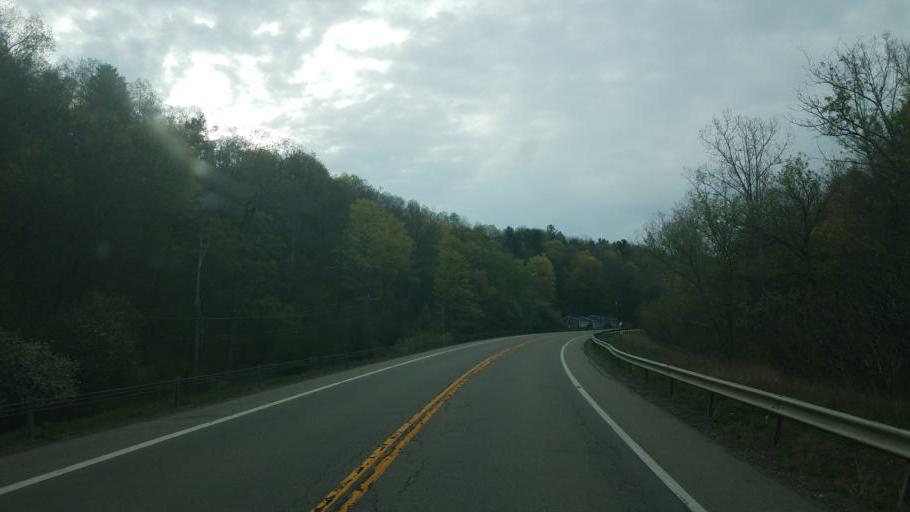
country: US
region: New York
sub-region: Steuben County
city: Canisteo
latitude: 42.1892
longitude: -77.5428
